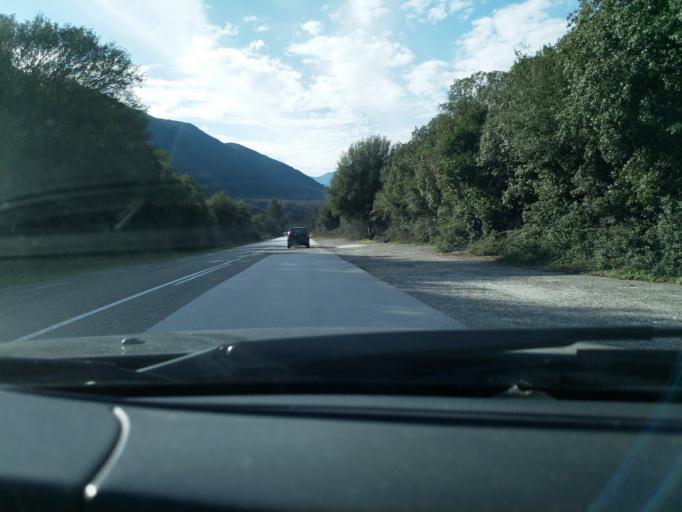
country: GR
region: Epirus
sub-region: Nomos Ioanninon
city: Agia Kyriaki
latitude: 39.4594
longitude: 20.8788
